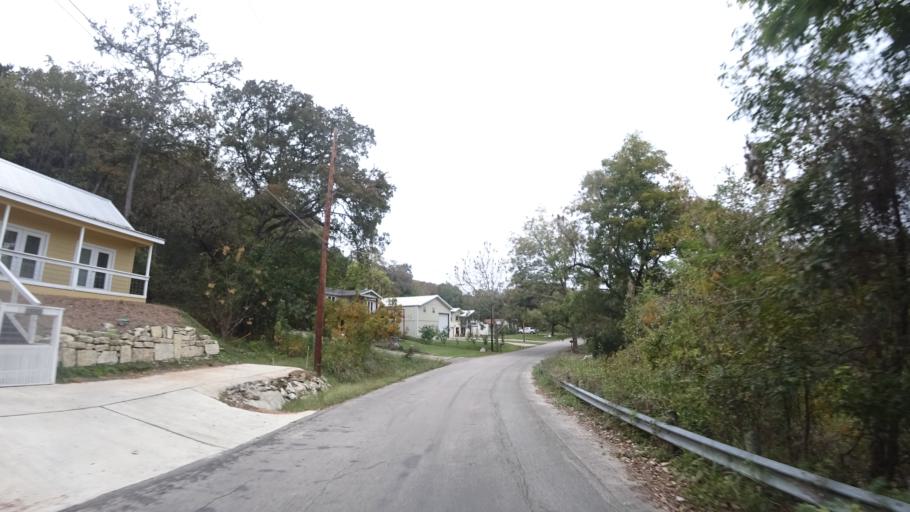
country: US
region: Texas
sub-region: Travis County
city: Hudson Bend
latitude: 30.3759
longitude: -97.9171
